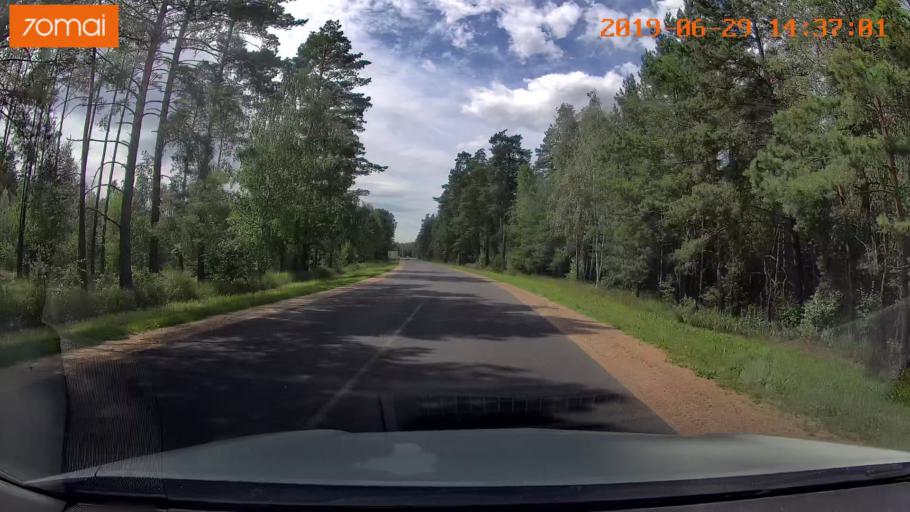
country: BY
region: Minsk
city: Starobin
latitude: 52.7500
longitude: 27.4729
